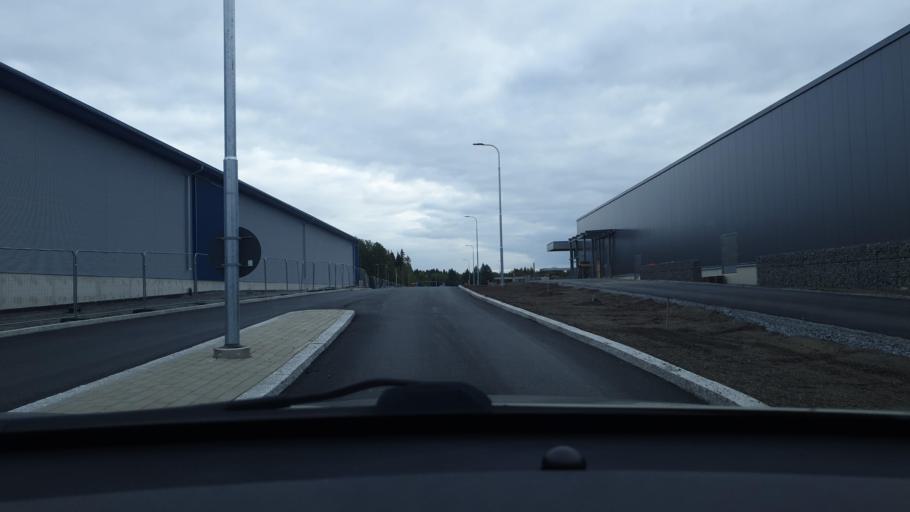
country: FI
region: Ostrobothnia
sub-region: Vaasa
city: Teeriniemi
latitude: 63.0737
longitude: 21.6995
